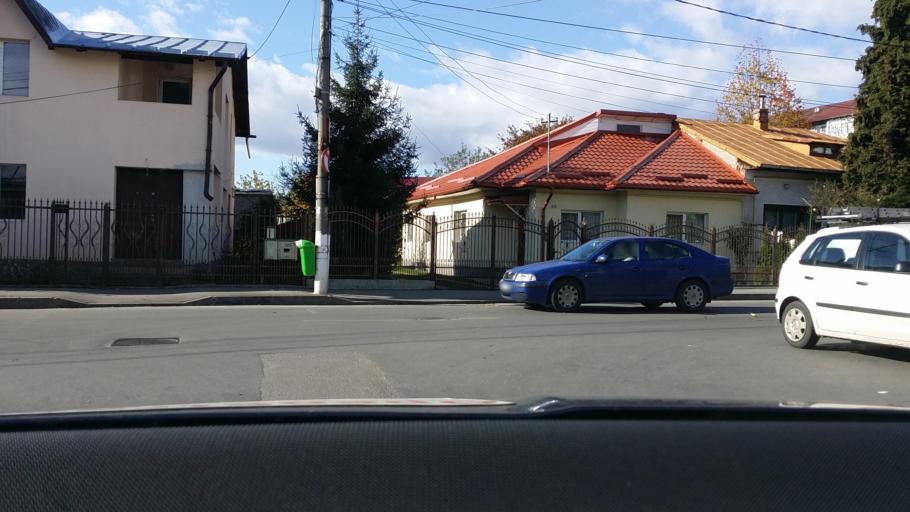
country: RO
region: Prahova
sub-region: Municipiul Campina
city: Campina
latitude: 45.1268
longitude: 25.7396
